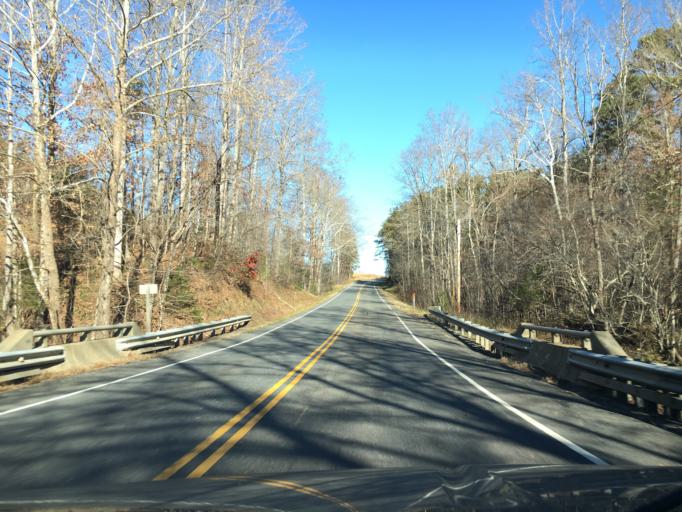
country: US
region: Virginia
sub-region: Buckingham County
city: Buckingham
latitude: 37.5116
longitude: -78.6180
